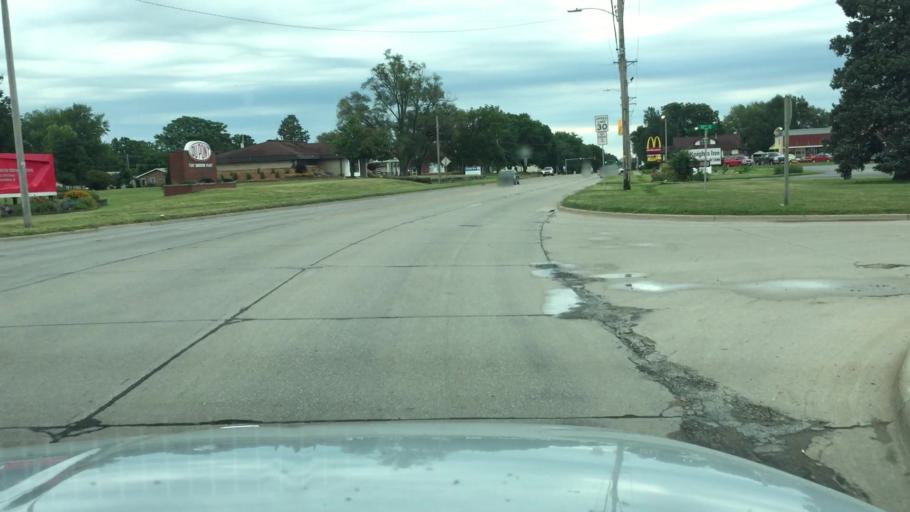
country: US
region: Iowa
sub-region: Lee County
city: Fort Madison
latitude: 40.6265
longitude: -91.3577
